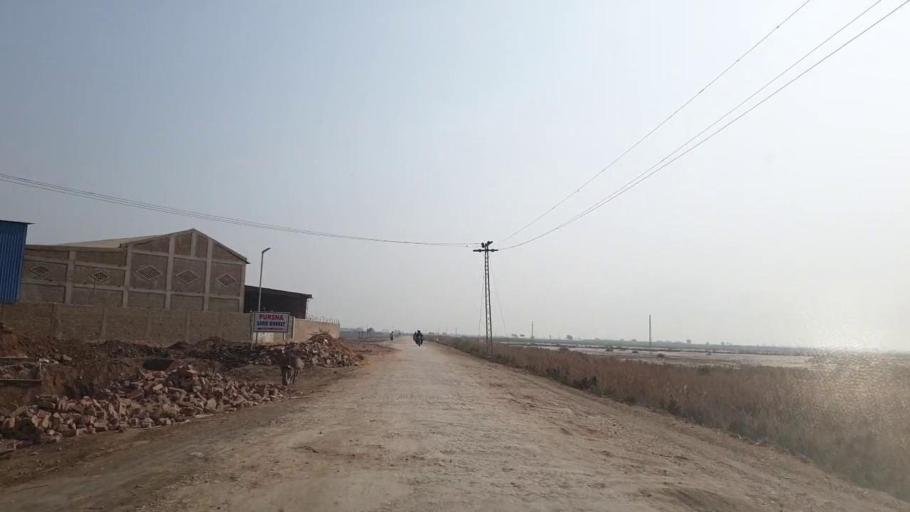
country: PK
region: Sindh
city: Mirpur Khas
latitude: 25.5483
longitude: 69.0473
